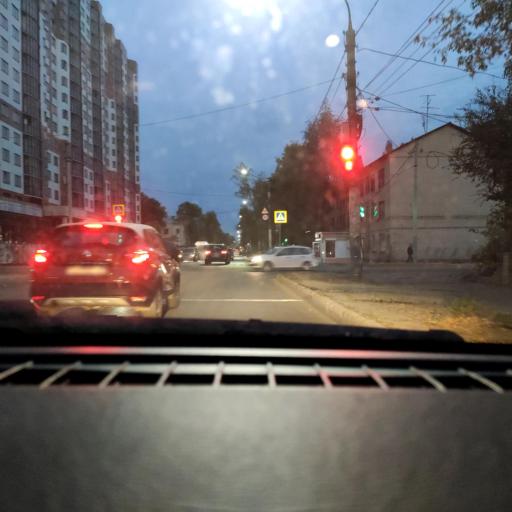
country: RU
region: Voronezj
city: Voronezh
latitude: 51.7228
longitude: 39.2658
